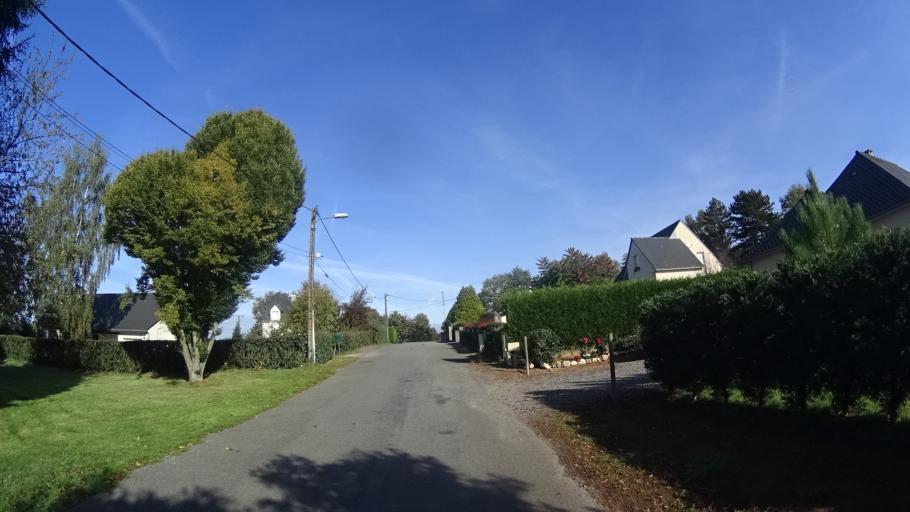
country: FR
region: Brittany
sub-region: Departement du Morbihan
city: Peillac
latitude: 47.7397
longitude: -2.2163
